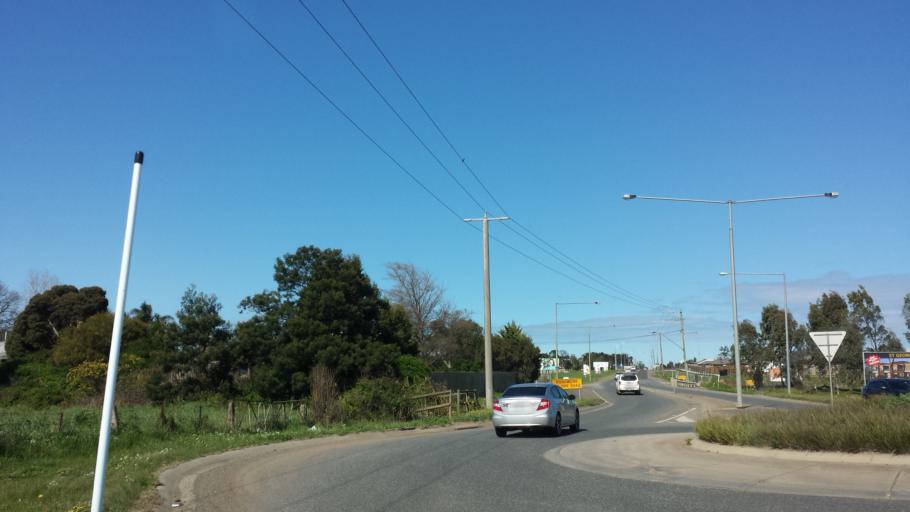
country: AU
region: Victoria
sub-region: Casey
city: Cranbourne East
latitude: -38.1026
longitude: 145.3304
